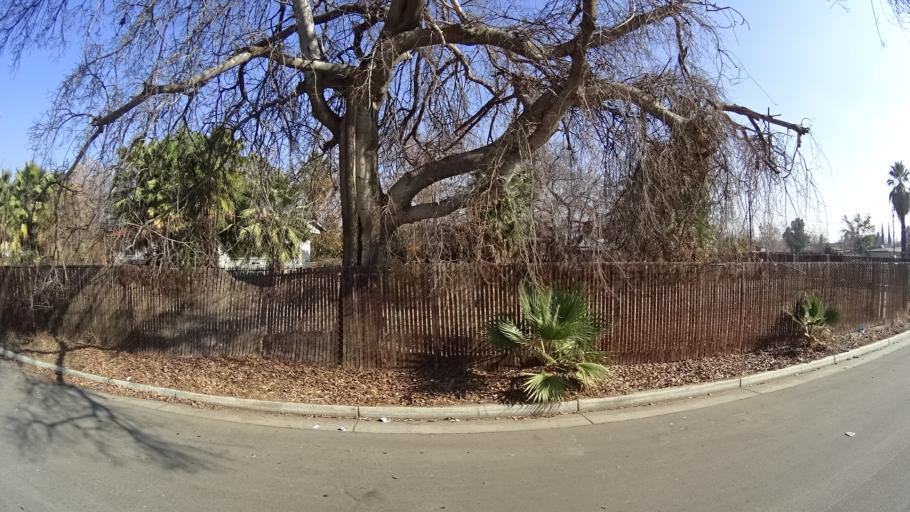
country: US
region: California
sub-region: Kern County
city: Bakersfield
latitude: 35.3669
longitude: -119.0107
